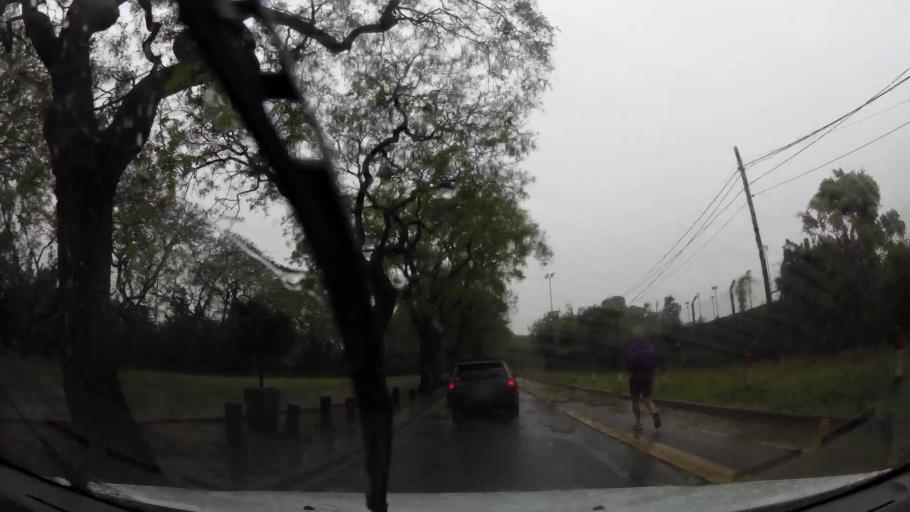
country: AR
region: Buenos Aires F.D.
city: Colegiales
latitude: -34.5618
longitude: -58.4341
